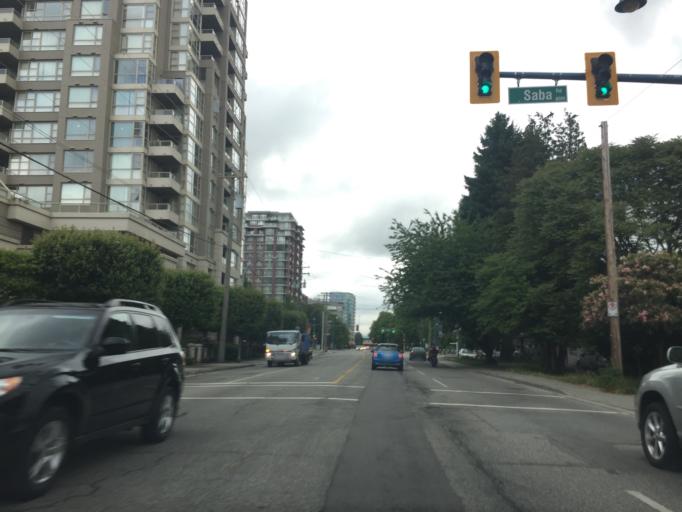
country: CA
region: British Columbia
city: Richmond
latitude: 49.1687
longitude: -123.1314
